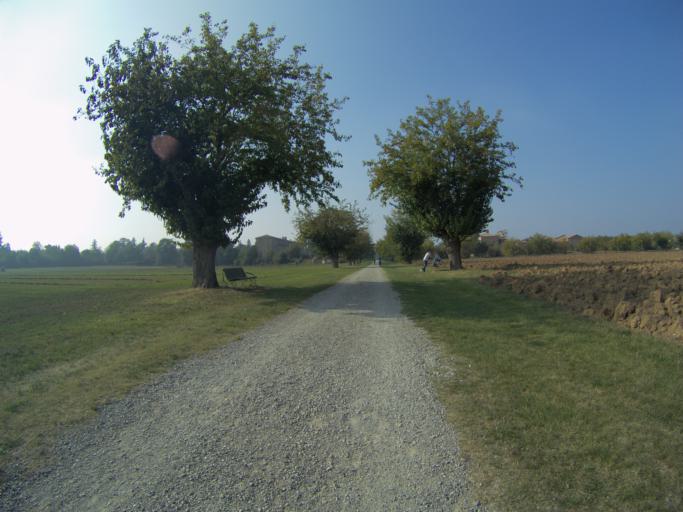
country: IT
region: Emilia-Romagna
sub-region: Provincia di Reggio Emilia
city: Forche
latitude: 44.6600
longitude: 10.5953
